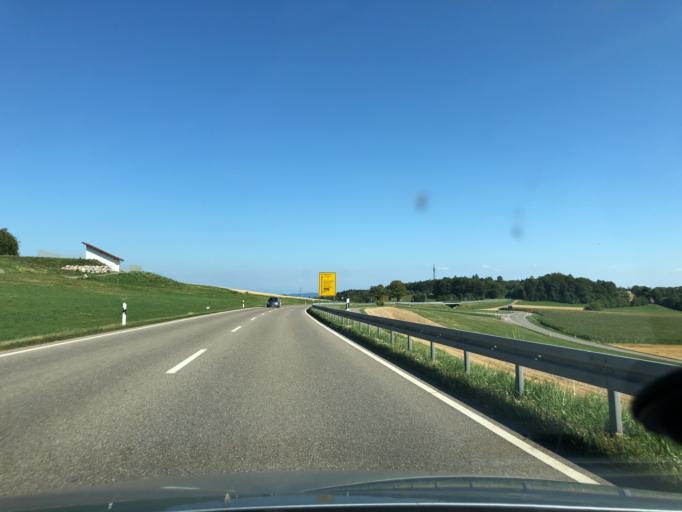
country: DE
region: Baden-Wuerttemberg
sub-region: Freiburg Region
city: Dogern
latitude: 47.6647
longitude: 8.1610
